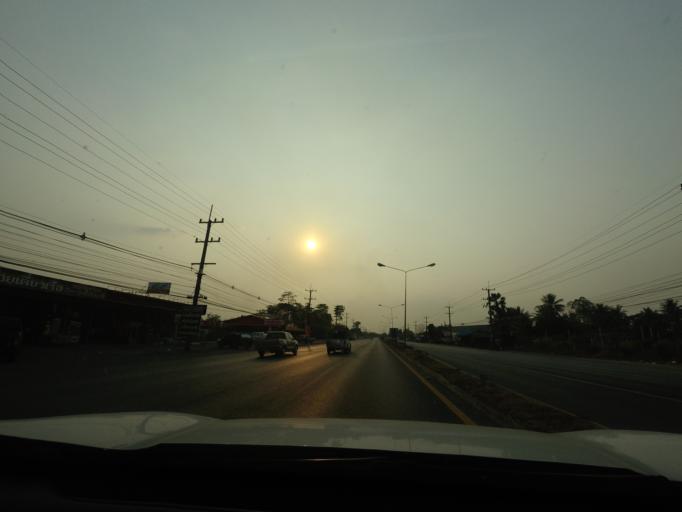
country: TH
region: Nakhon Nayok
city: Pak Phli
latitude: 14.1478
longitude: 101.2863
